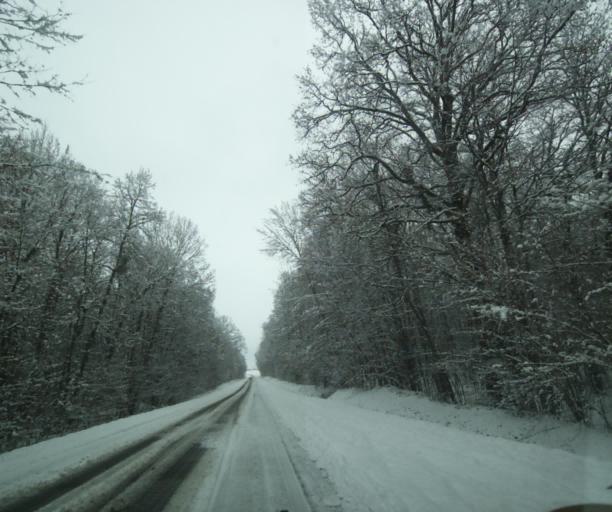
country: FR
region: Champagne-Ardenne
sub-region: Departement de la Haute-Marne
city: Montier-en-Der
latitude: 48.5268
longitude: 4.7960
